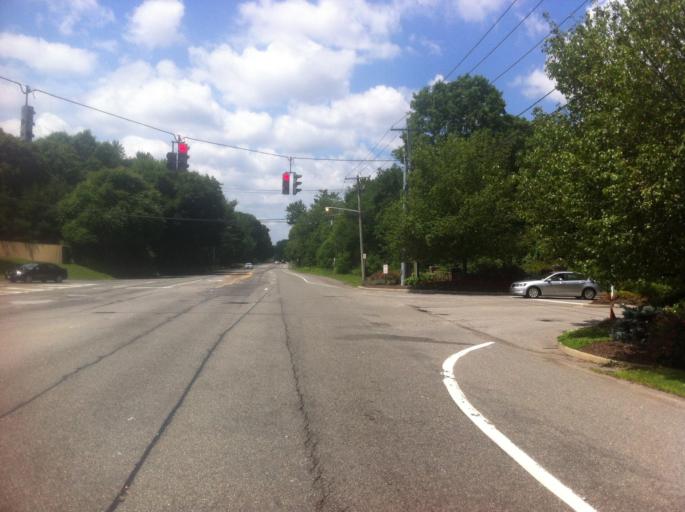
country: US
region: New York
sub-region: Nassau County
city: Old Brookville
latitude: 40.8211
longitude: -73.5979
